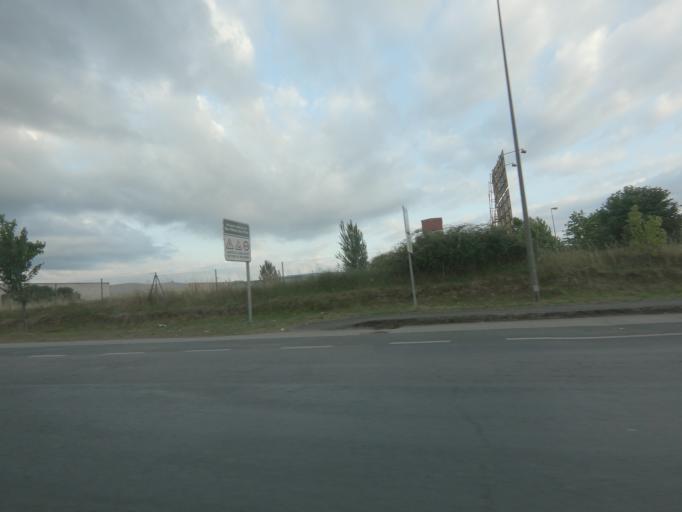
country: ES
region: Galicia
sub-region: Provincia de Ourense
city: Taboadela
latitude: 42.2881
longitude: -7.8271
